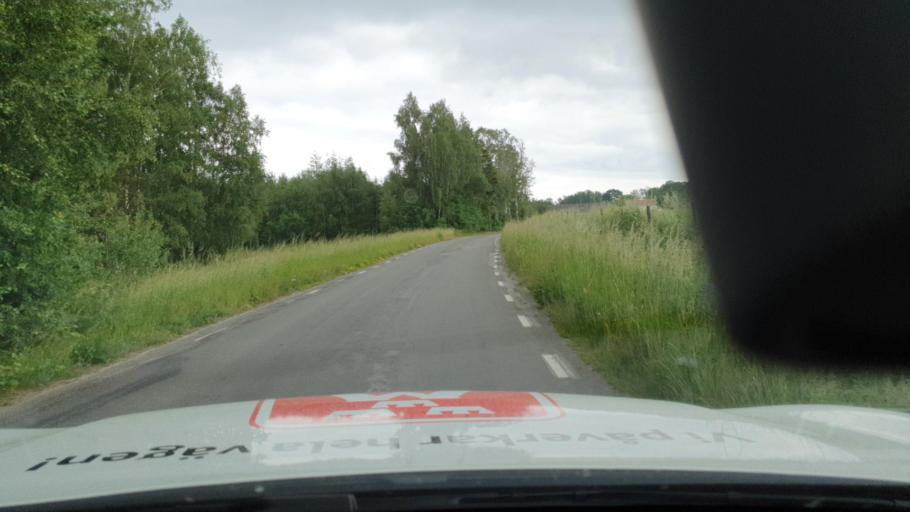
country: SE
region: Vaestra Goetaland
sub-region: Hjo Kommun
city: Hjo
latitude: 58.1741
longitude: 14.1951
